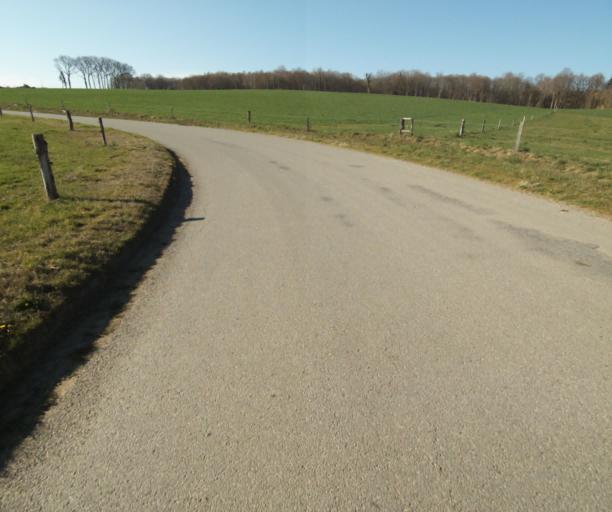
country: FR
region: Limousin
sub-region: Departement de la Correze
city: Chamboulive
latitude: 45.4756
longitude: 1.7190
